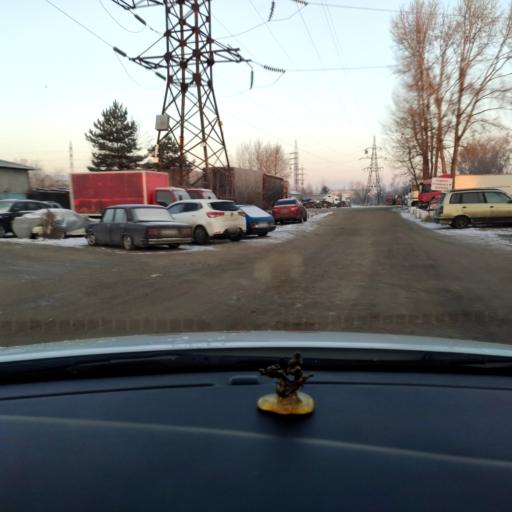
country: RU
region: Tatarstan
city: Staroye Arakchino
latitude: 55.8301
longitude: 49.0302
